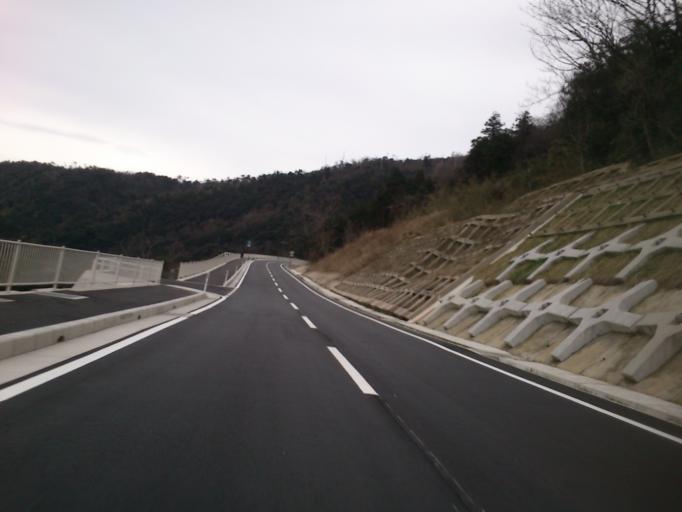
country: JP
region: Kyoto
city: Miyazu
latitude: 35.7468
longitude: 135.2537
